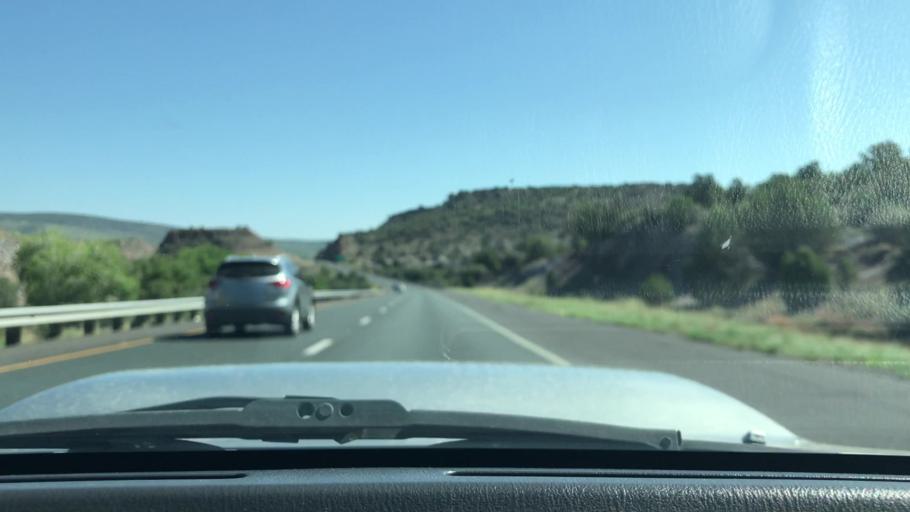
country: US
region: Arizona
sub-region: Yavapai County
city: Camp Verde
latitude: 34.4958
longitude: -112.0035
